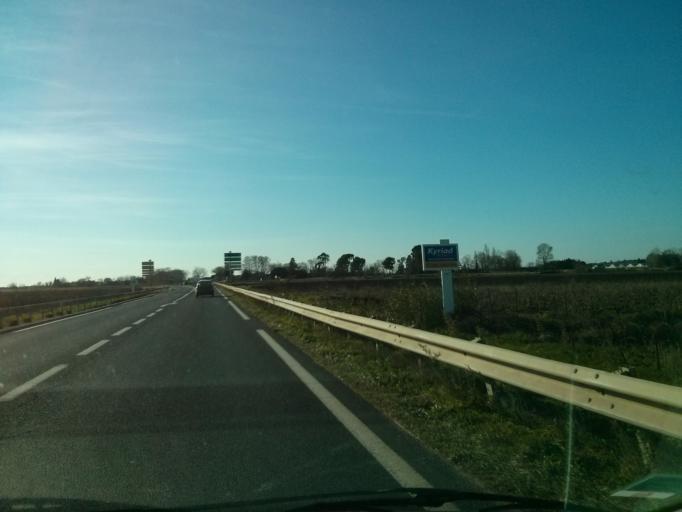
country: FR
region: Languedoc-Roussillon
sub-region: Departement du Gard
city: Gallargues-le-Montueux
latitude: 43.6962
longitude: 4.1713
